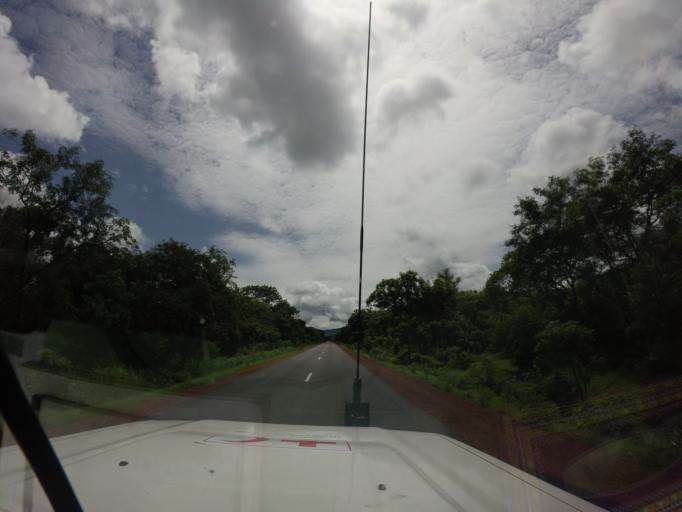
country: SL
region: Northern Province
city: Gberia Fotombu
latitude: 10.1423
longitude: -11.1721
